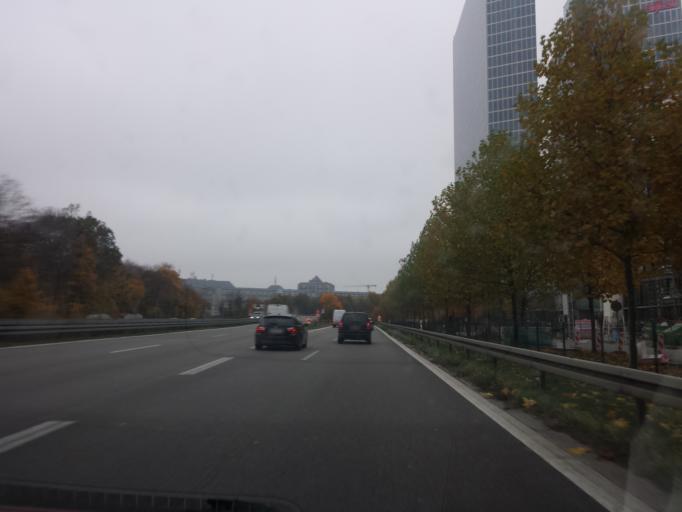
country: DE
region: Bavaria
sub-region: Upper Bavaria
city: Bogenhausen
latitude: 48.1780
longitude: 11.5947
